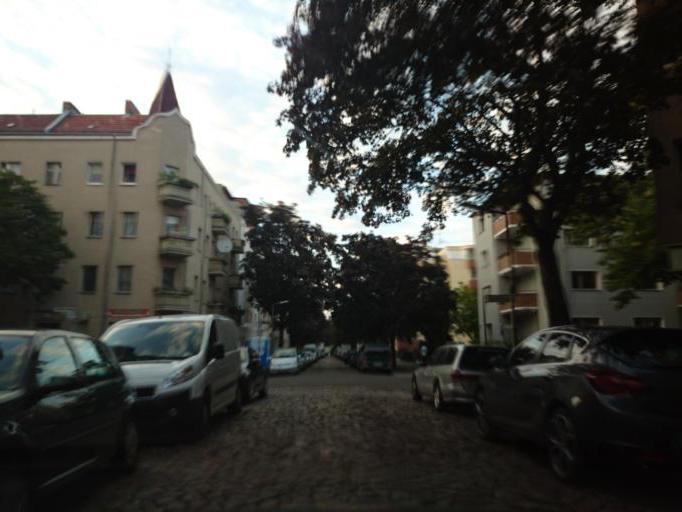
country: DE
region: Berlin
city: Tegel
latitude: 52.5698
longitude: 13.3099
